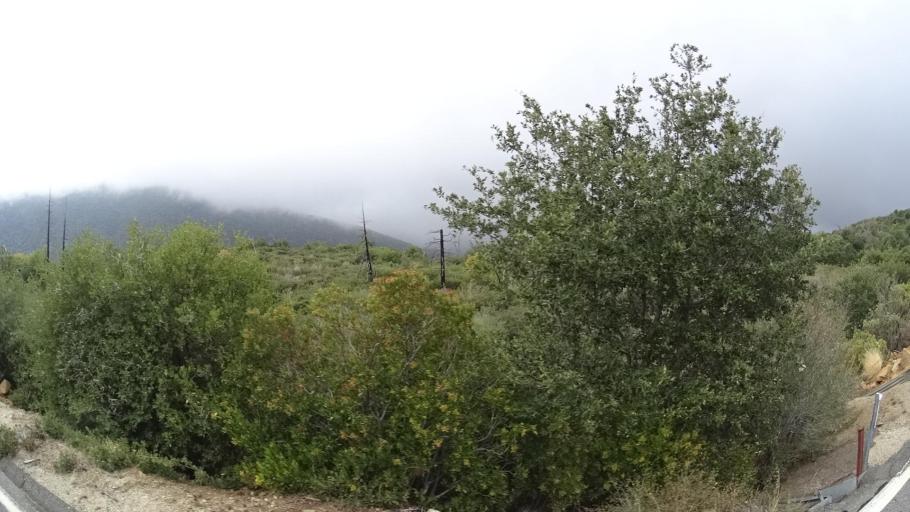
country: US
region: California
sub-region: San Diego County
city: Julian
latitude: 33.0006
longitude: -116.5981
